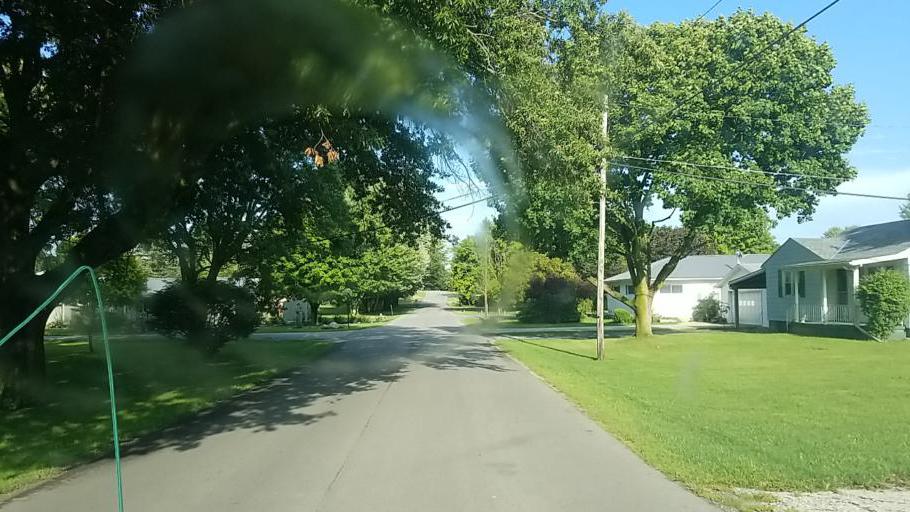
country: US
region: Ohio
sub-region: Wyandot County
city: Upper Sandusky
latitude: 40.8355
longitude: -83.2777
